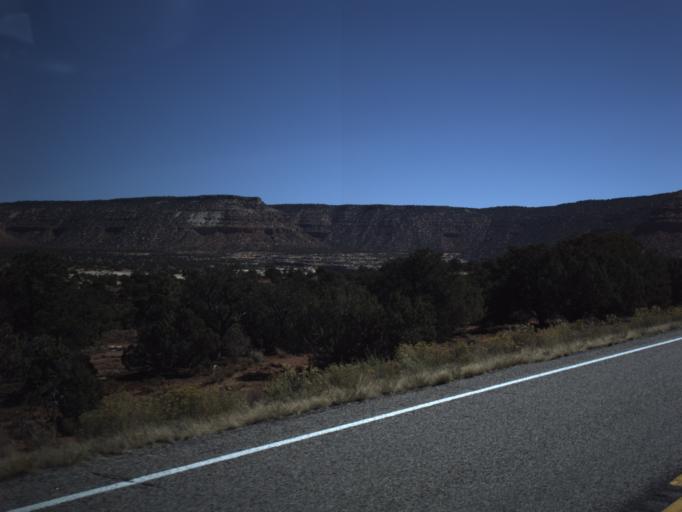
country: US
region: Utah
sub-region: San Juan County
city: Blanding
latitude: 37.6316
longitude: -110.0912
